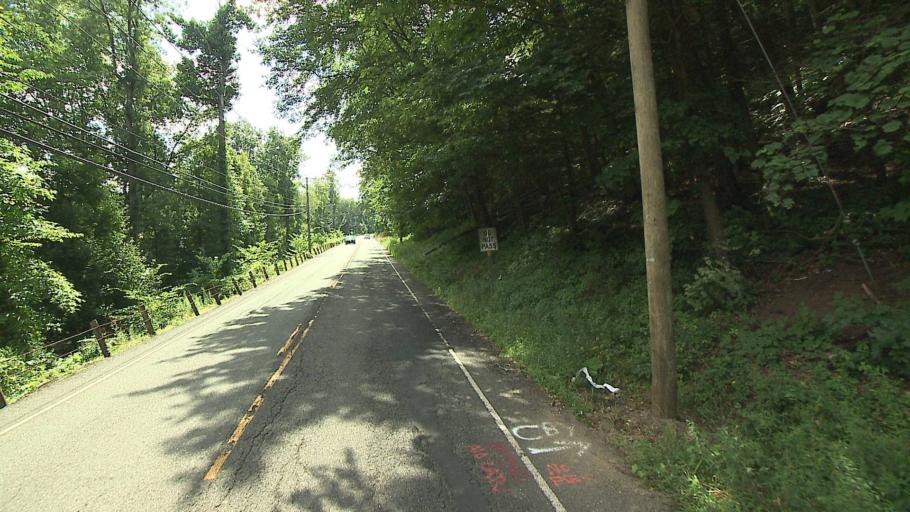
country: US
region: Connecticut
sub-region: Fairfield County
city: Sherman
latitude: 41.5613
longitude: -73.4920
